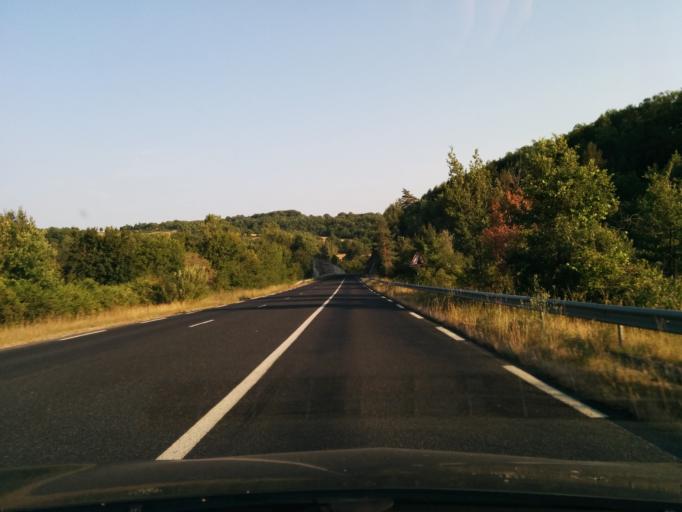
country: FR
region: Midi-Pyrenees
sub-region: Departement du Lot
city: Le Vigan
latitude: 44.7136
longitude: 1.4826
